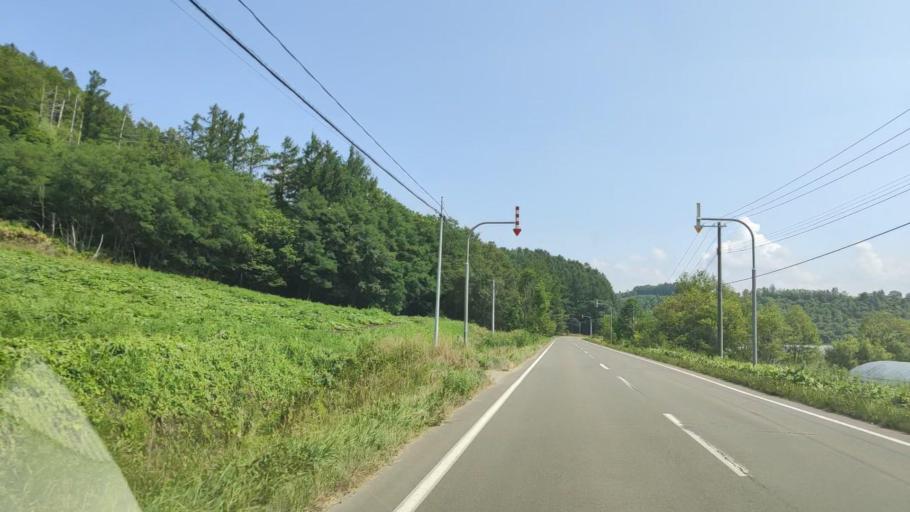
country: JP
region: Hokkaido
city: Shimo-furano
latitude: 43.4287
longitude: 142.4065
